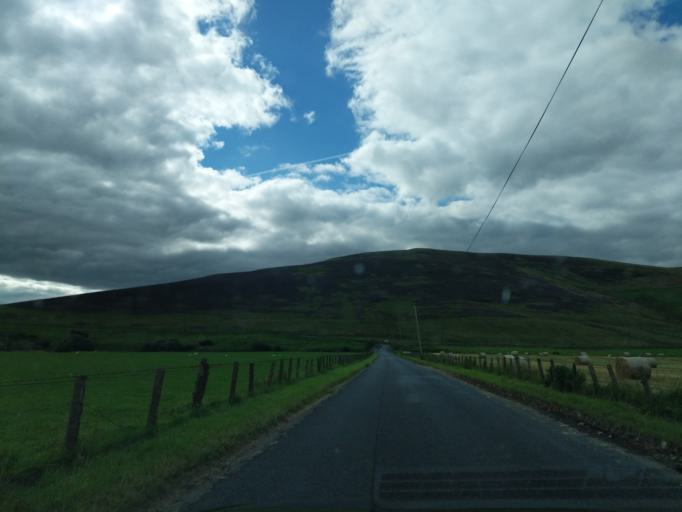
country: GB
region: Scotland
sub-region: The Scottish Borders
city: West Linton
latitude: 55.6751
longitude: -3.3308
